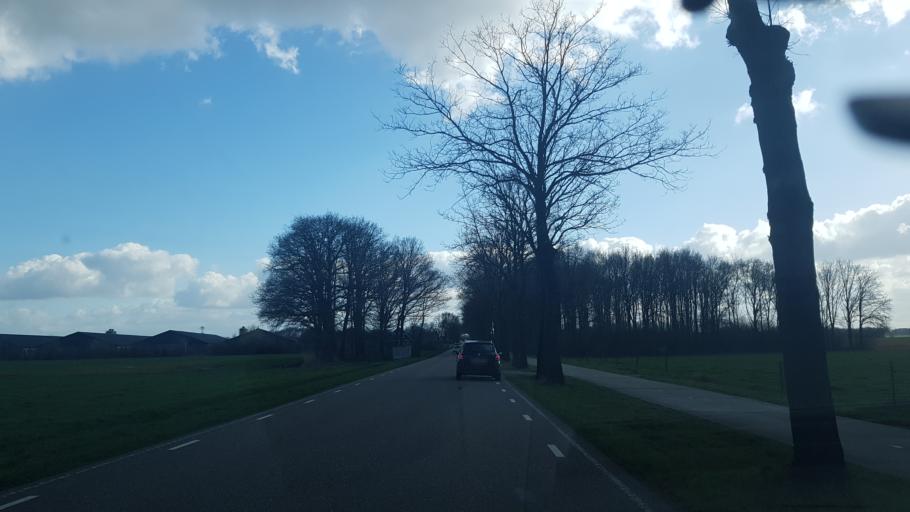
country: NL
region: North Brabant
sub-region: Gemeente Eersel
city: Eersel
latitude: 51.3870
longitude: 5.2987
